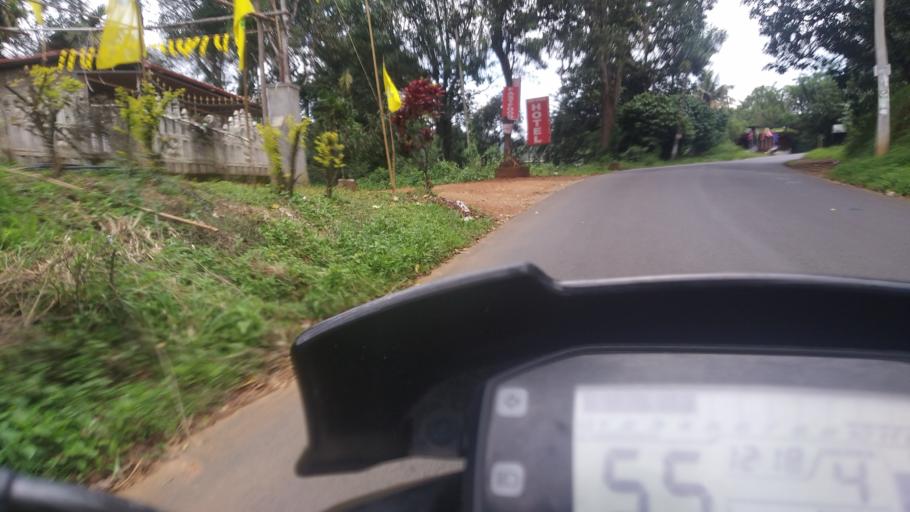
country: IN
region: Kerala
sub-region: Idukki
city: Munnar
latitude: 10.0190
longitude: 77.0056
